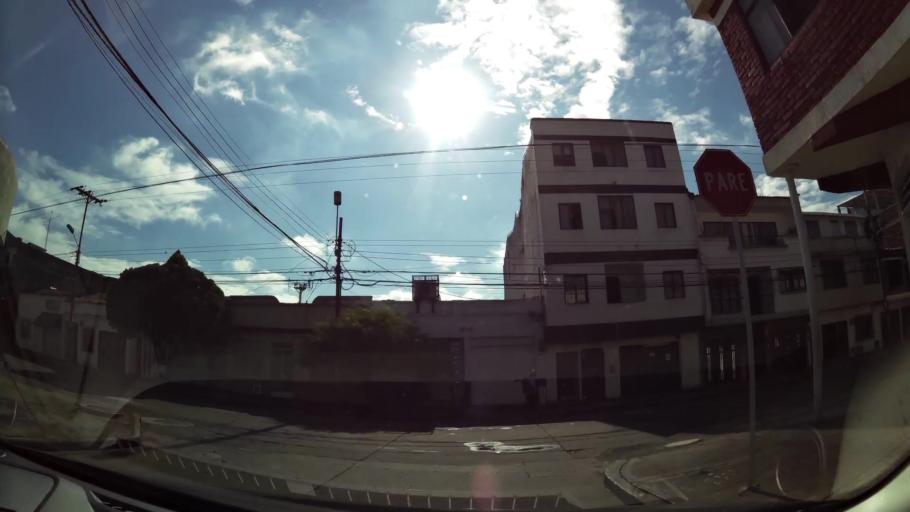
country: CO
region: Valle del Cauca
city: Cali
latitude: 3.4351
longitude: -76.5325
